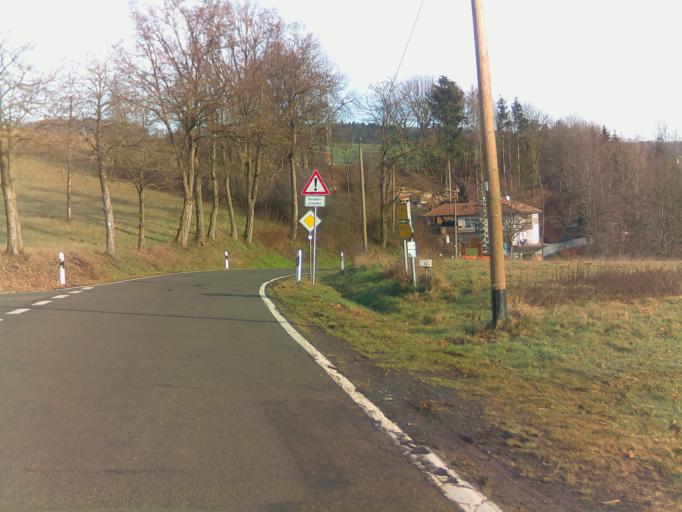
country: DE
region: Rheinland-Pfalz
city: Borsborn
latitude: 49.4336
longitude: 7.3921
